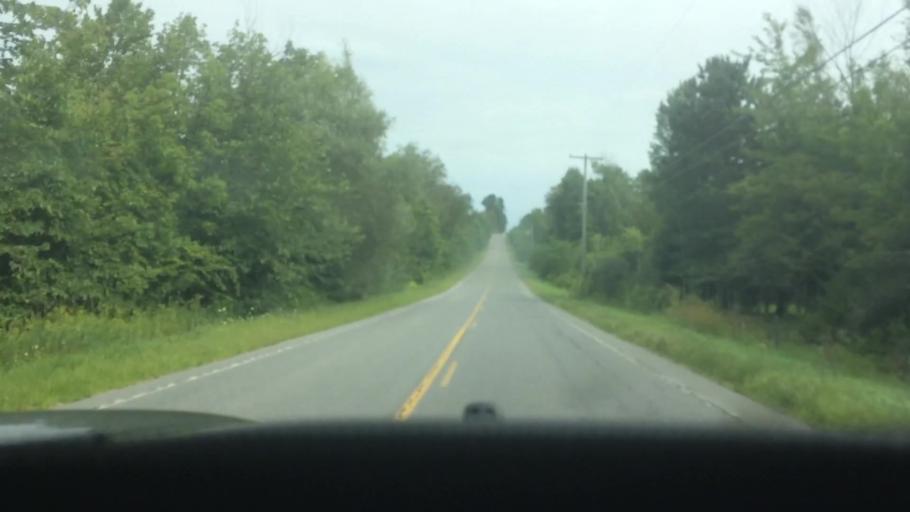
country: US
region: New York
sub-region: St. Lawrence County
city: Canton
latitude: 44.4786
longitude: -75.2244
